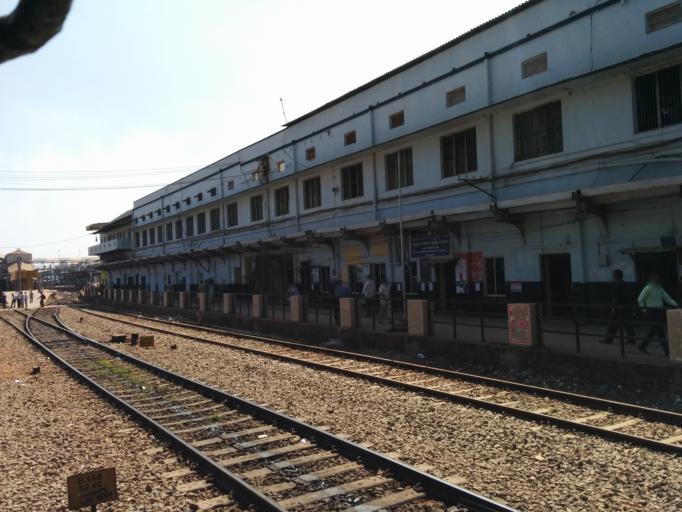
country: IN
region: Karnataka
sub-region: Dharwad
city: Hubli
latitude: 15.3523
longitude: 75.1468
